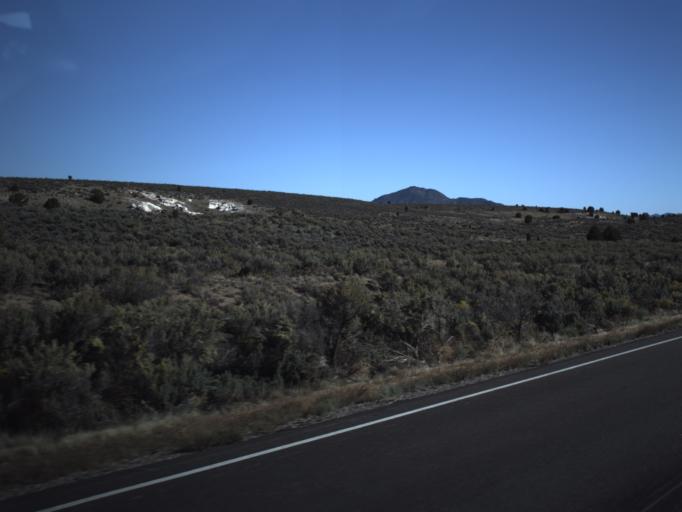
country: US
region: Utah
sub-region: Washington County
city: Enterprise
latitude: 37.7342
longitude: -114.0229
